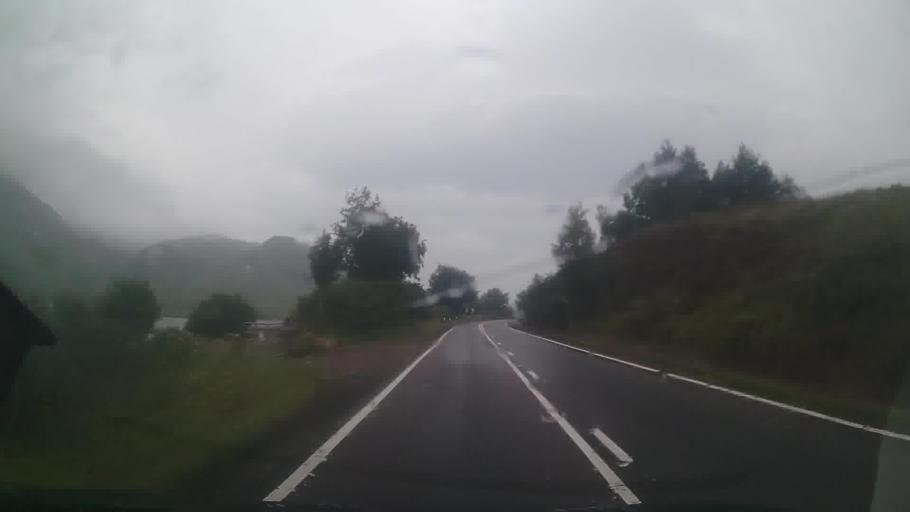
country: GB
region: Scotland
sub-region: Highland
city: Fort William
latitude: 56.8781
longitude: -5.5758
